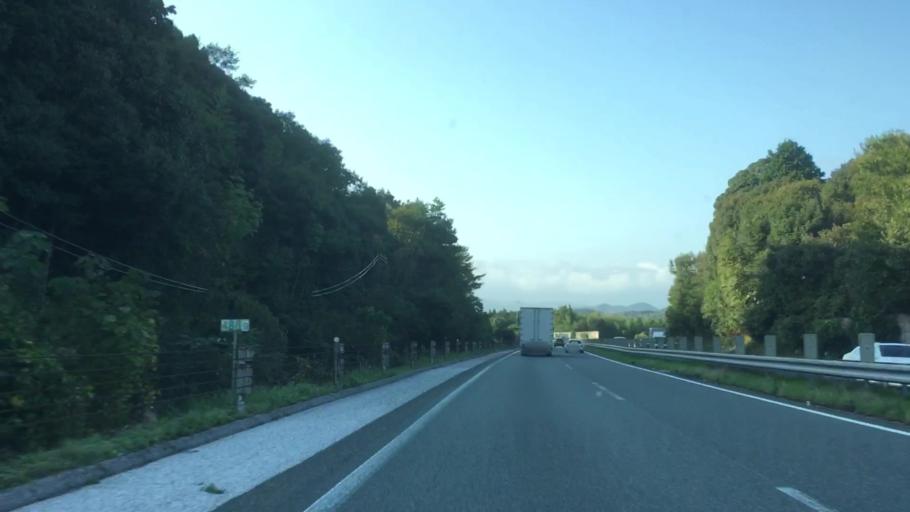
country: JP
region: Yamaguchi
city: Ogori-shimogo
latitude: 34.1487
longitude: 131.3431
